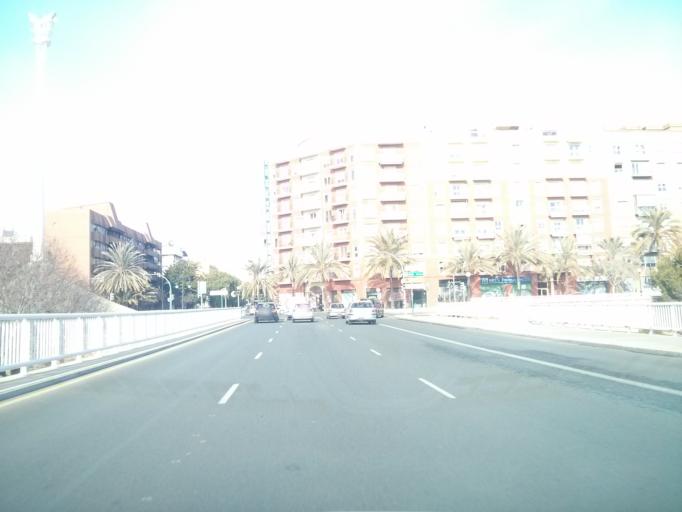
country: ES
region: Valencia
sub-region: Provincia de Valencia
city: Valencia
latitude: 39.4813
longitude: -0.3833
